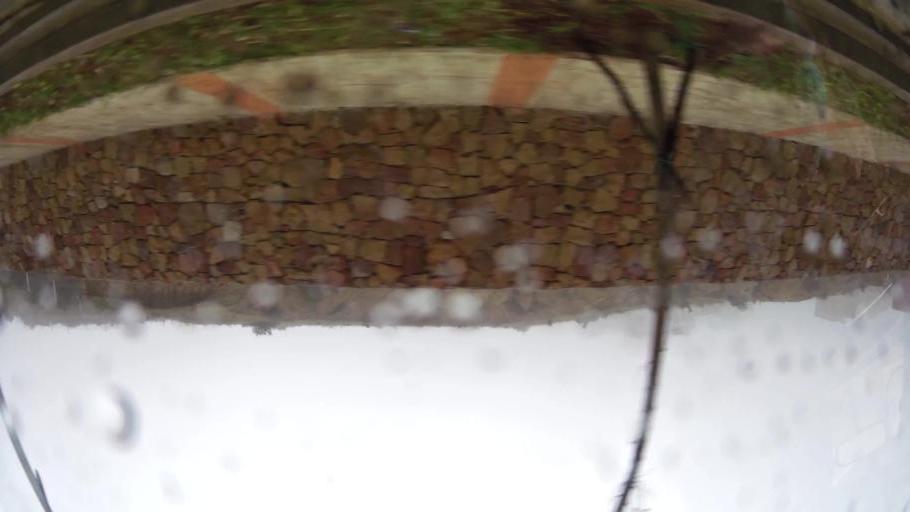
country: MA
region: Taza-Al Hoceima-Taounate
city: Tirhanimine
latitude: 35.2339
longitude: -3.9541
